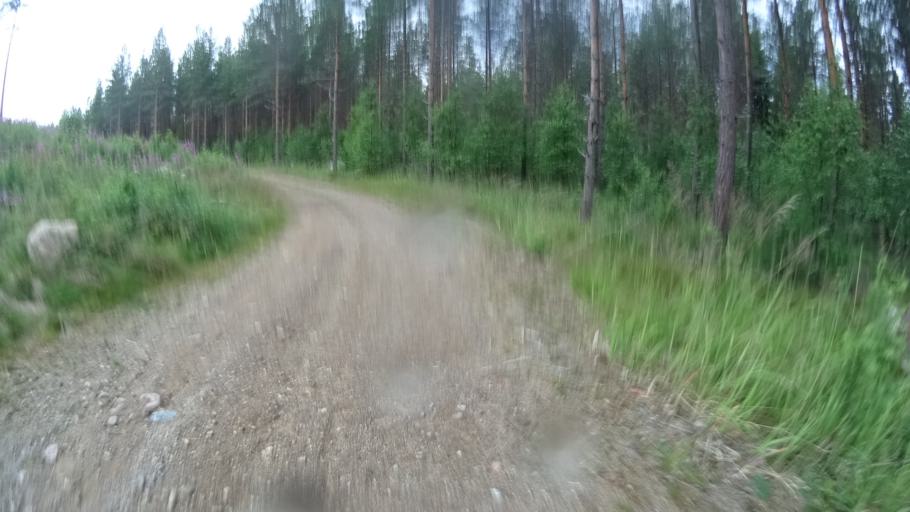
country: FI
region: Uusimaa
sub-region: Helsinki
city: Karkkila
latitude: 60.5962
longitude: 24.1822
